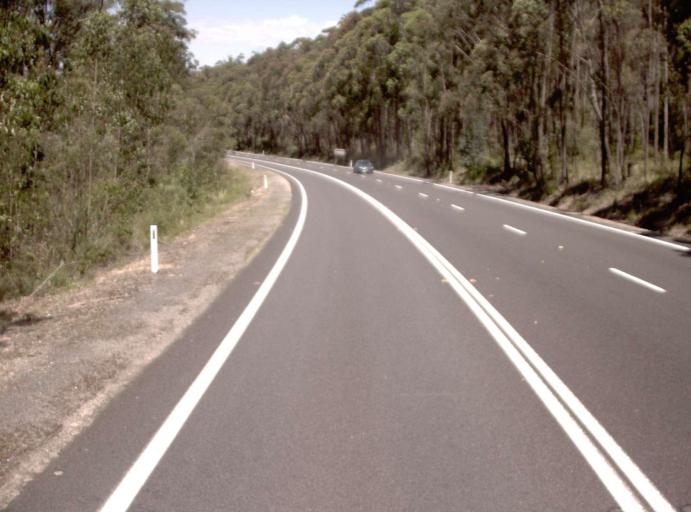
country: AU
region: Victoria
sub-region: East Gippsland
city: Lakes Entrance
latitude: -37.7093
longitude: 148.6538
